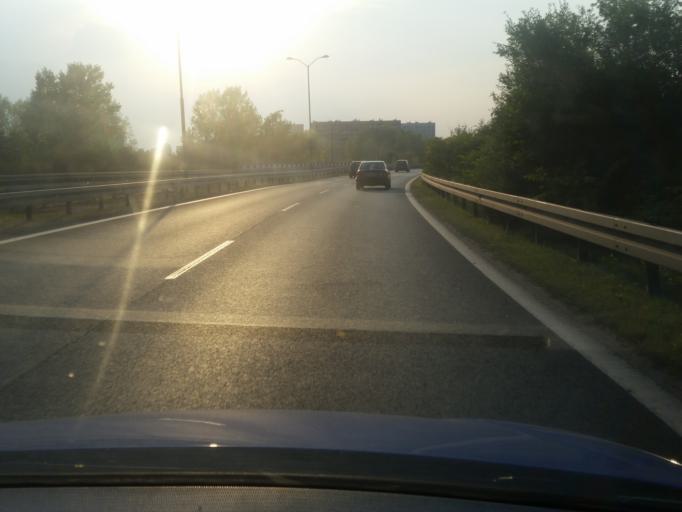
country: PL
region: Silesian Voivodeship
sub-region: Katowice
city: Katowice
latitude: 50.2593
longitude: 19.0686
